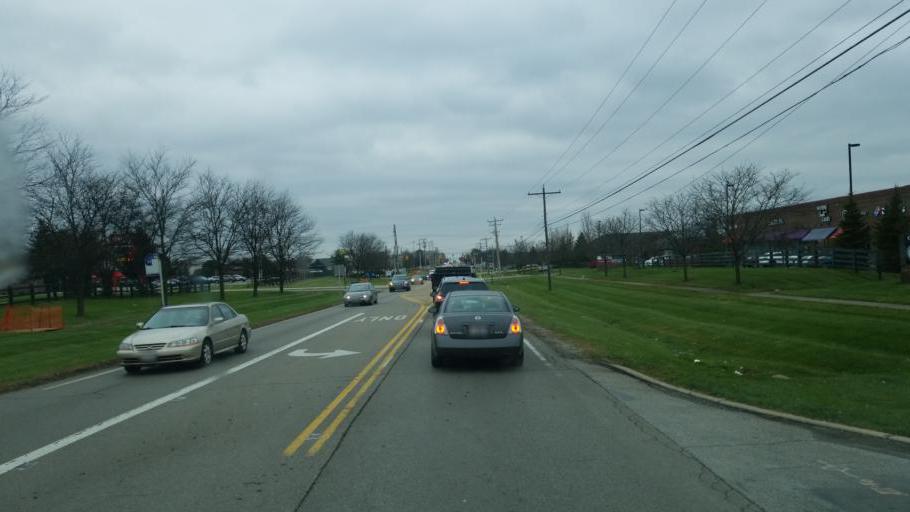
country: US
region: Ohio
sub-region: Franklin County
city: Gahanna
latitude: 40.0601
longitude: -82.8634
